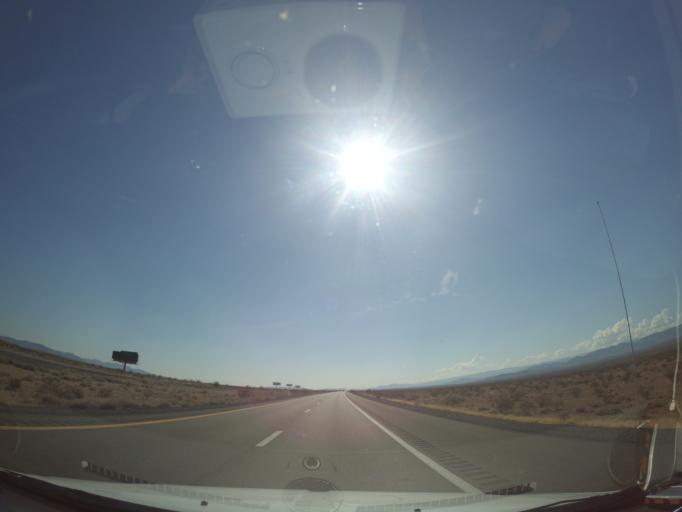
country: US
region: Nevada
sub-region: Clark County
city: Moapa Town
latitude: 36.5798
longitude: -114.6576
